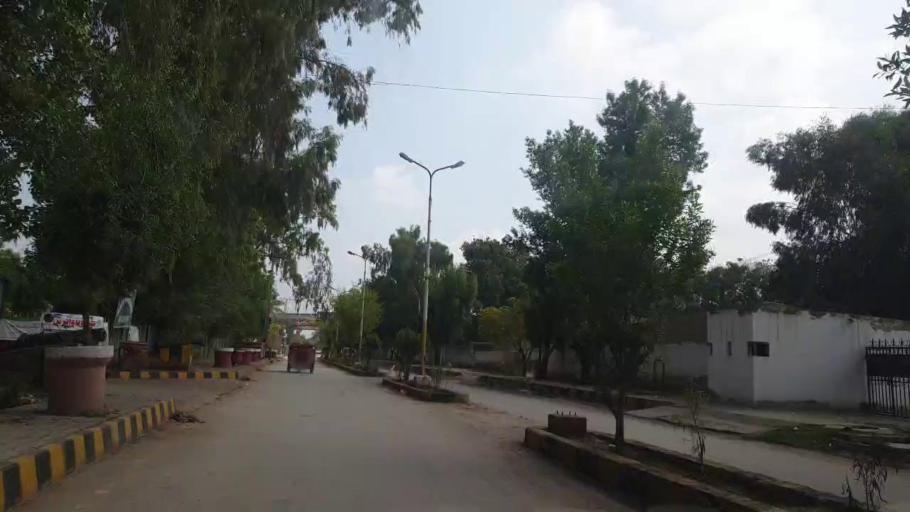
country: PK
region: Sindh
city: Khairpur
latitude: 27.5409
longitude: 68.7563
